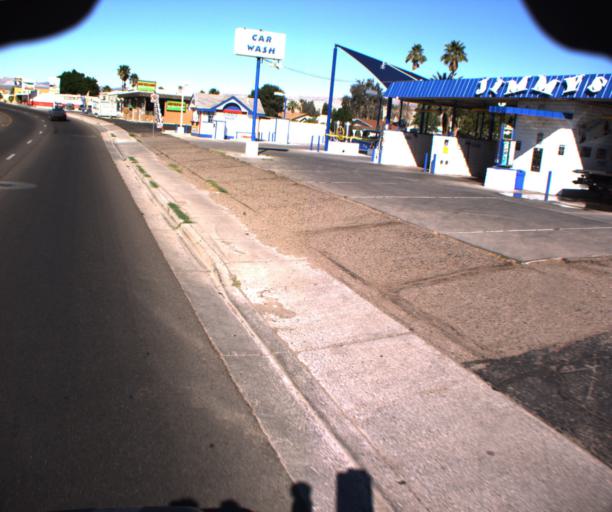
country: US
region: Arizona
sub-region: Mohave County
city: Bullhead City
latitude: 35.1190
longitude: -114.5960
